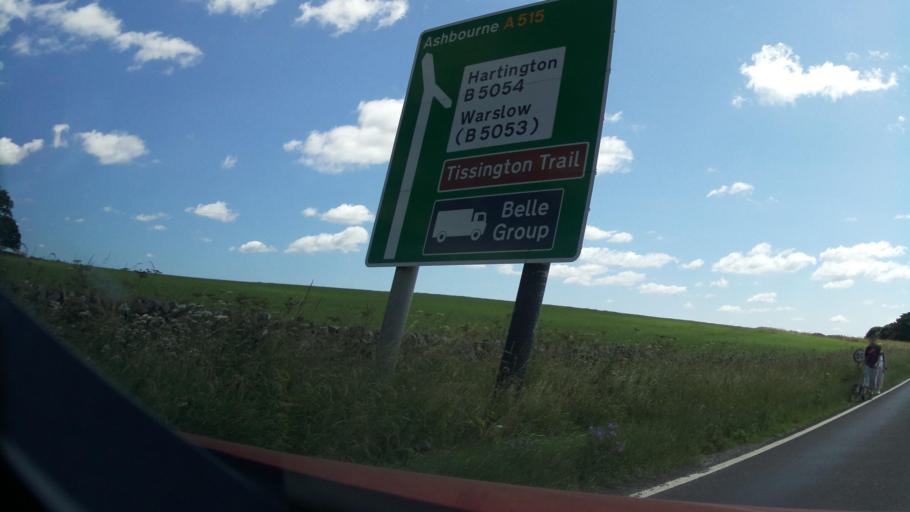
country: GB
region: England
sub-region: Derbyshire
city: Bakewell
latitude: 53.1491
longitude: -1.7661
